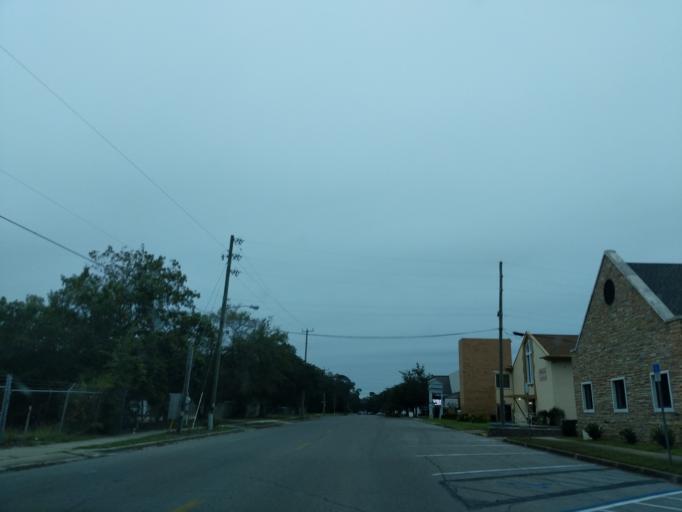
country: US
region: Florida
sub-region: Okaloosa County
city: Fort Walton Beach
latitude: 30.4053
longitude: -86.6089
